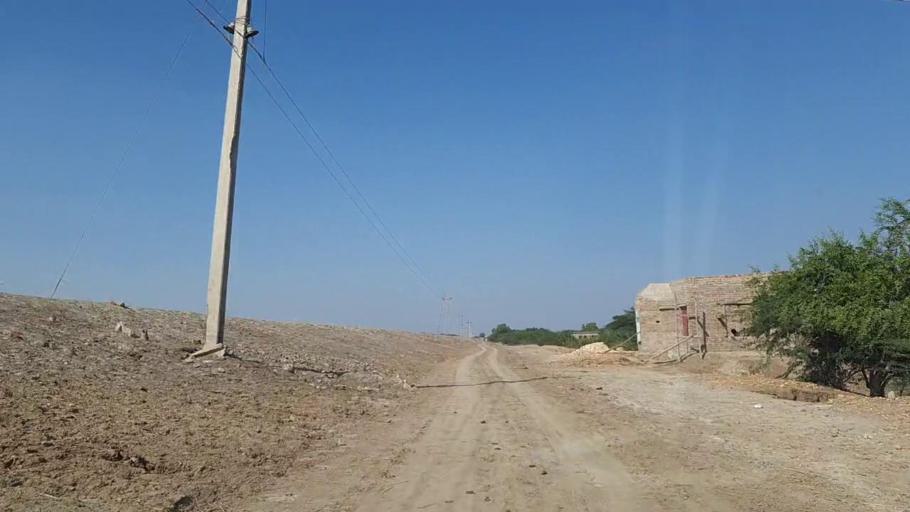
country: PK
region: Sindh
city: Chuhar Jamali
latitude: 24.5412
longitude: 68.0157
